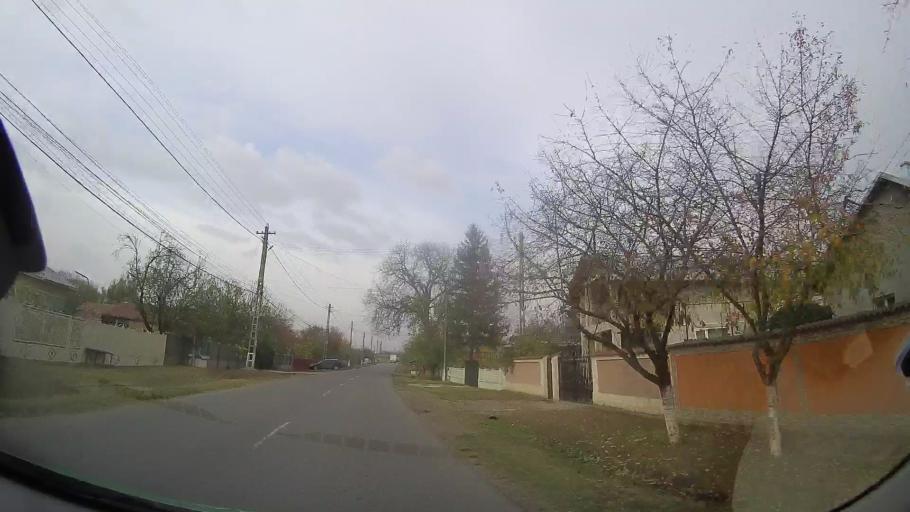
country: RO
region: Prahova
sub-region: Comuna Gorgota
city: Potigrafu
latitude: 44.7793
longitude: 26.1032
